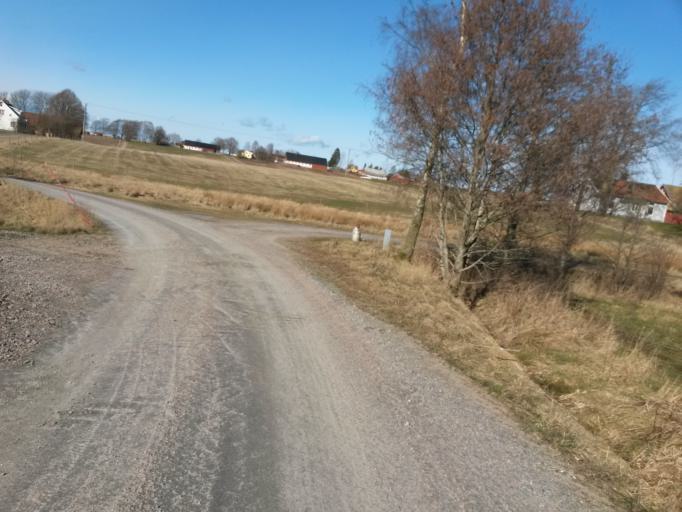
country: SE
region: Vaestra Goetaland
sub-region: Vargarda Kommun
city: Jonstorp
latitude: 57.9750
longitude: 12.6566
